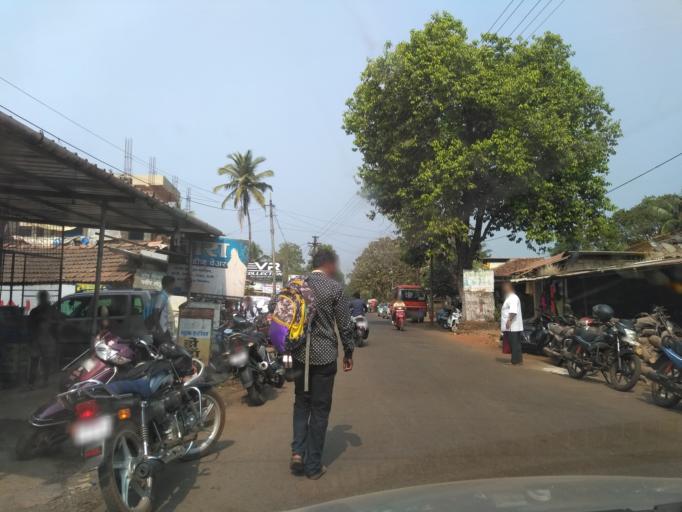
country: IN
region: Goa
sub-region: North Goa
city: Dicholi
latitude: 15.6809
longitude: 73.9682
